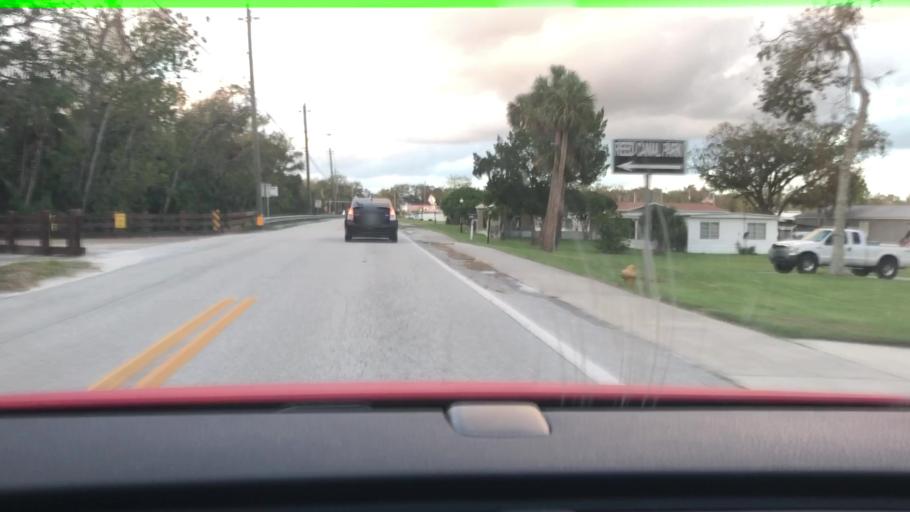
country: US
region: Florida
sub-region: Volusia County
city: South Daytona
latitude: 29.1559
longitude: -81.0162
